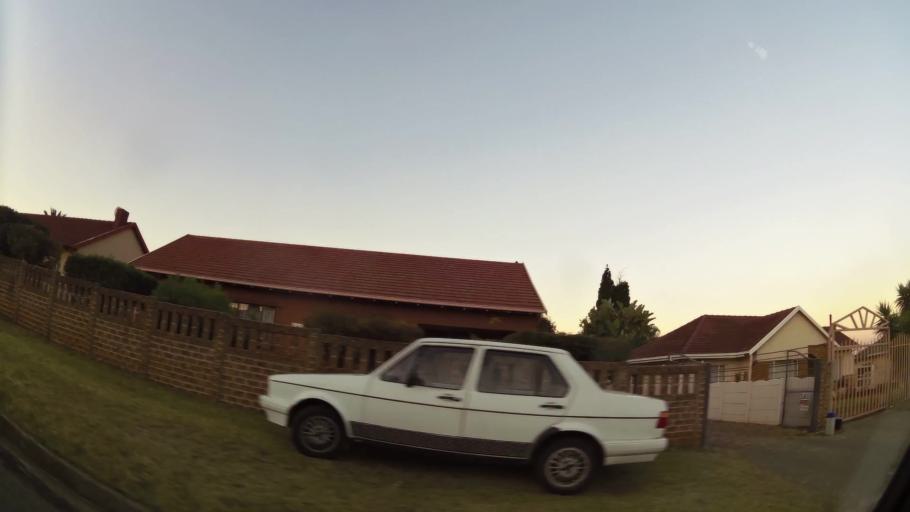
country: ZA
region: Gauteng
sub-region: Ekurhuleni Metropolitan Municipality
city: Germiston
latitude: -26.2629
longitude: 28.1609
